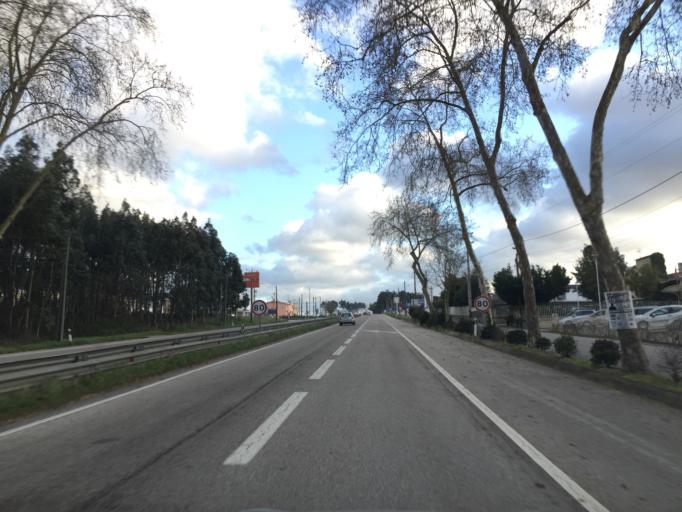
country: PT
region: Leiria
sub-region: Batalha
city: Batalha
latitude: 39.6836
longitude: -8.8347
